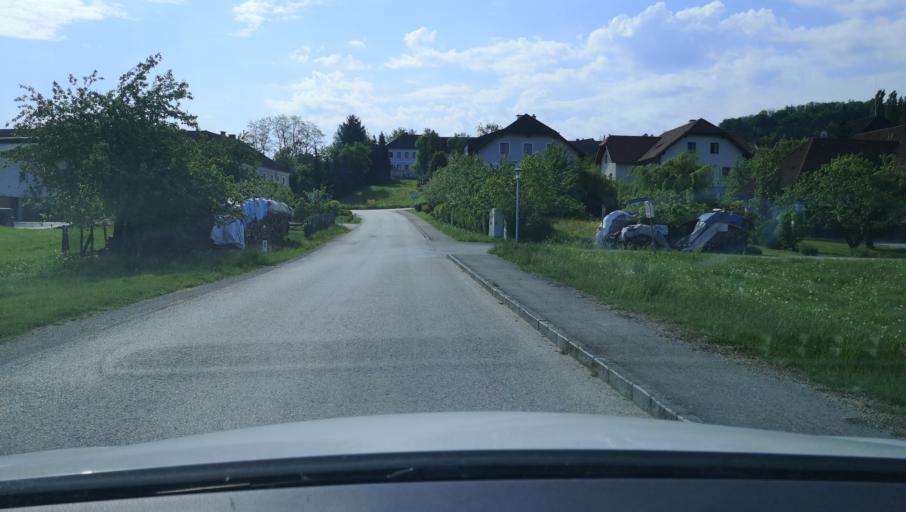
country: AT
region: Lower Austria
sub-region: Politischer Bezirk Amstetten
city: Neuhofen an der Ybbs
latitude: 48.0586
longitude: 14.8617
